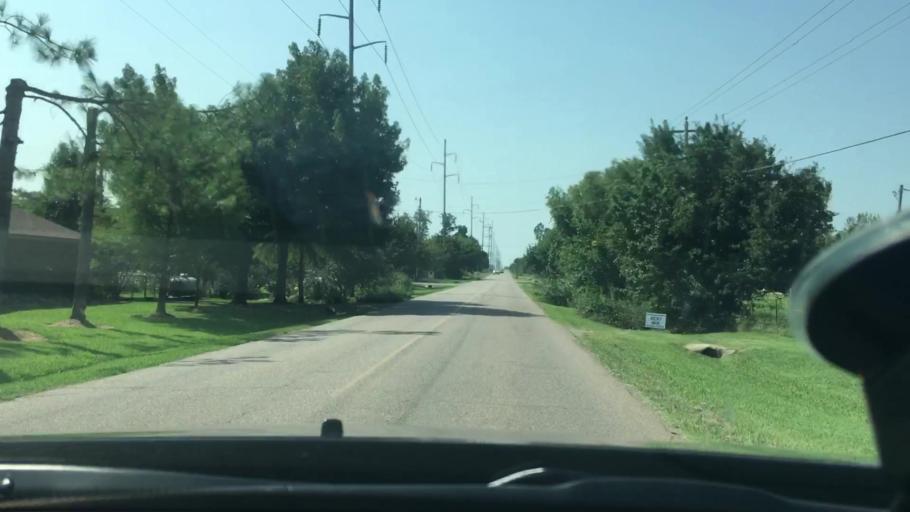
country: US
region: Oklahoma
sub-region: Bryan County
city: Durant
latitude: 34.0100
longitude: -96.4253
